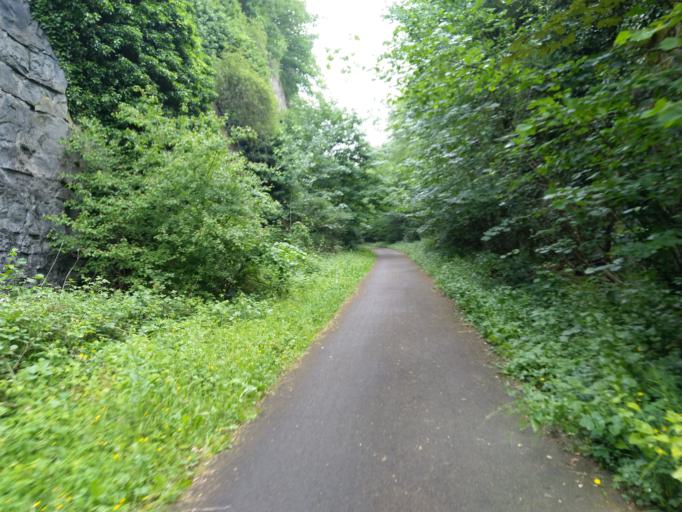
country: BE
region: Wallonia
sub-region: Province de Namur
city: Mettet
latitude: 50.3008
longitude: 4.7515
